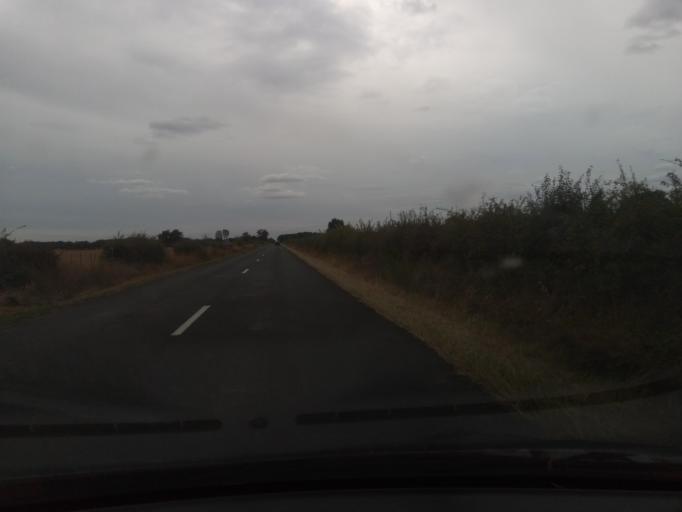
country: FR
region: Poitou-Charentes
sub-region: Departement de la Vienne
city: Pleumartin
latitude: 46.6635
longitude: 0.7989
